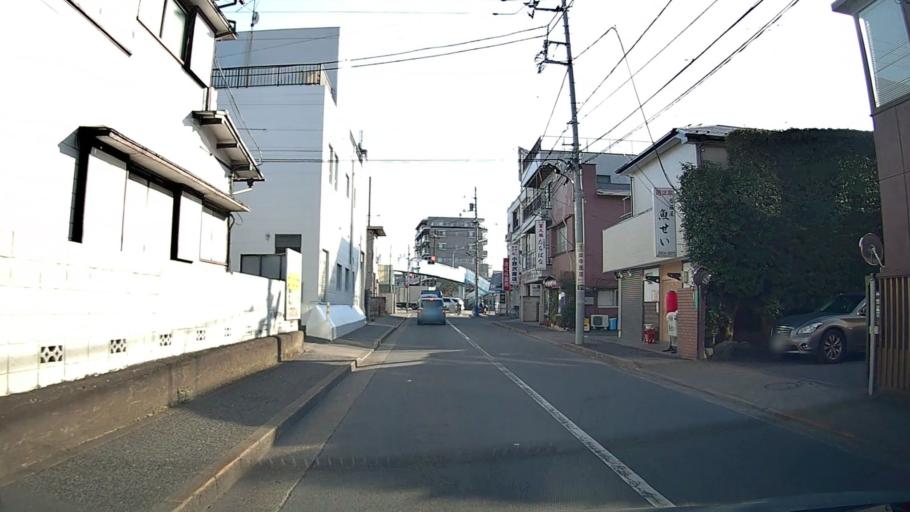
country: JP
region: Saitama
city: Wako
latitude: 35.7552
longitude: 139.6078
